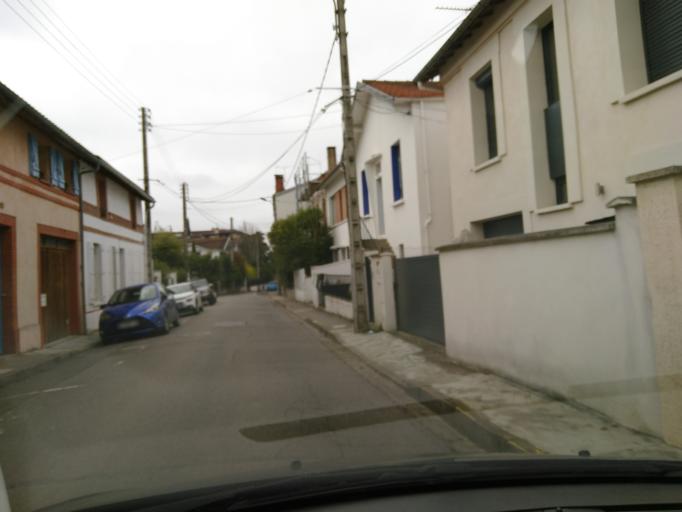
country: FR
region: Midi-Pyrenees
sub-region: Departement de la Haute-Garonne
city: Toulouse
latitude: 43.5917
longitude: 1.4648
